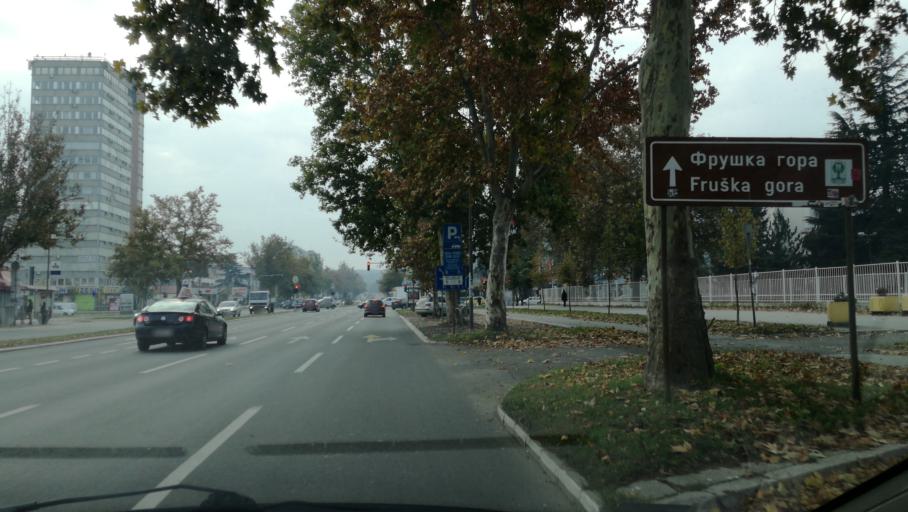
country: RS
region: Autonomna Pokrajina Vojvodina
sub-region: Juznobacki Okrug
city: Novi Sad
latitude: 45.2449
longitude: 19.8407
